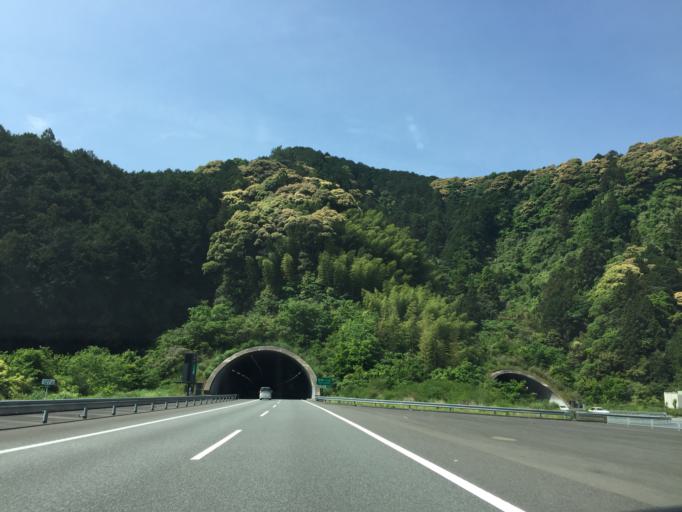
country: JP
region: Shizuoka
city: Shizuoka-shi
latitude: 35.0018
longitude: 138.3067
